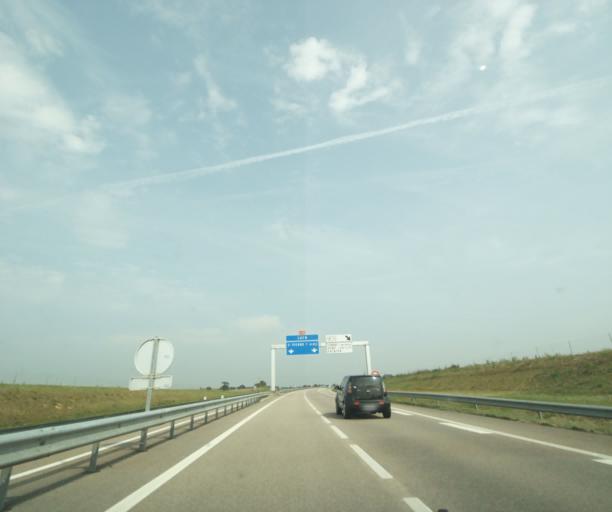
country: FR
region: Lower Normandy
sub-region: Departement du Calvados
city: Falaise
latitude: 48.8827
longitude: -0.2204
